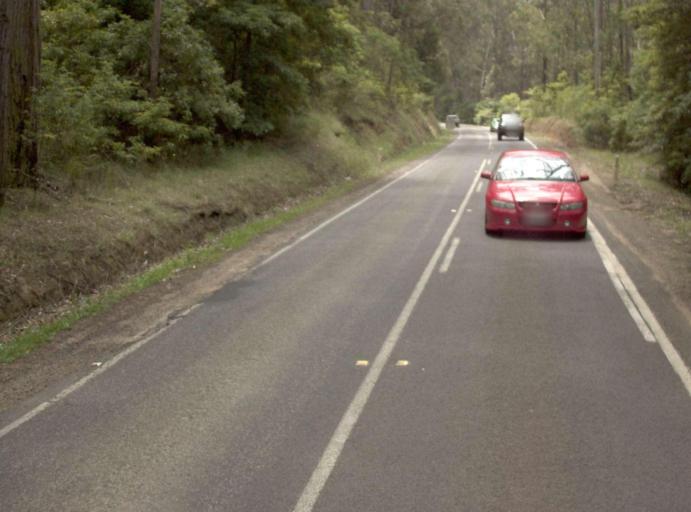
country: AU
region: Victoria
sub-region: Latrobe
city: Traralgon
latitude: -38.4301
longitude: 146.7408
